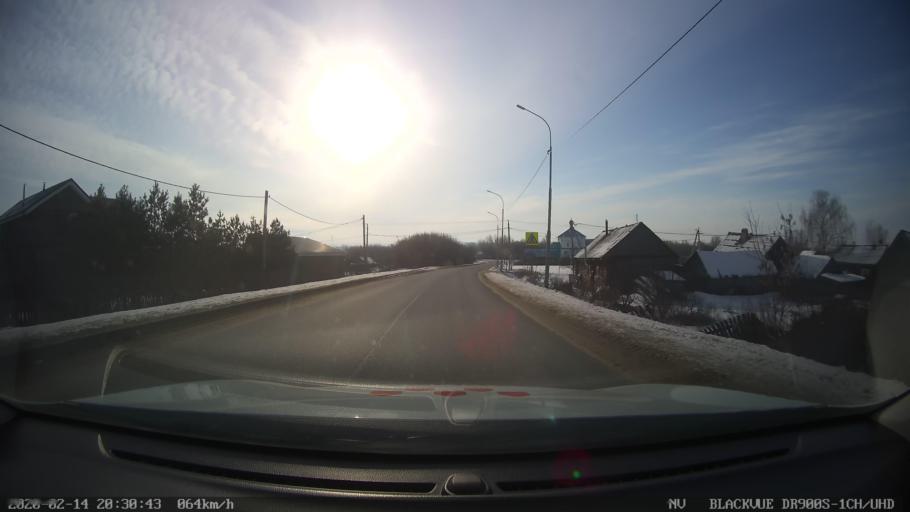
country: RU
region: Tatarstan
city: Stolbishchi
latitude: 55.4409
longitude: 48.9917
